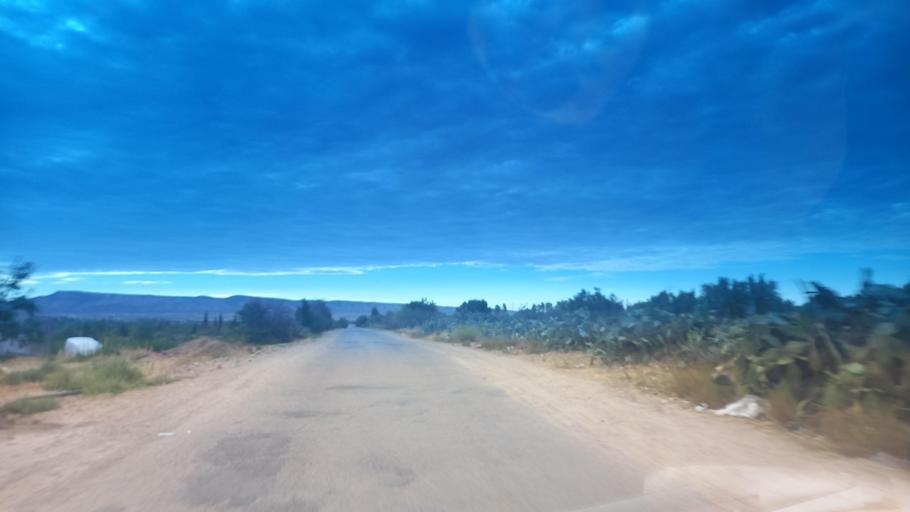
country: TN
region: Al Qasrayn
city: Sbiba
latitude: 35.3777
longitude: 9.0627
